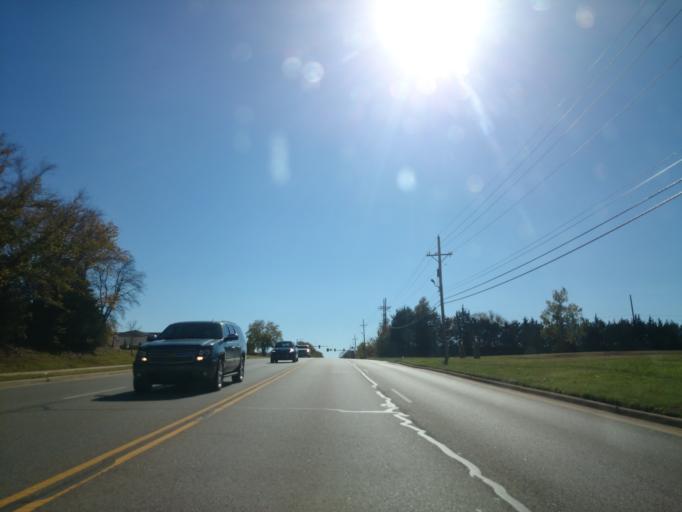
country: US
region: Oklahoma
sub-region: Payne County
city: Stillwater
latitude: 36.1714
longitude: -97.0698
